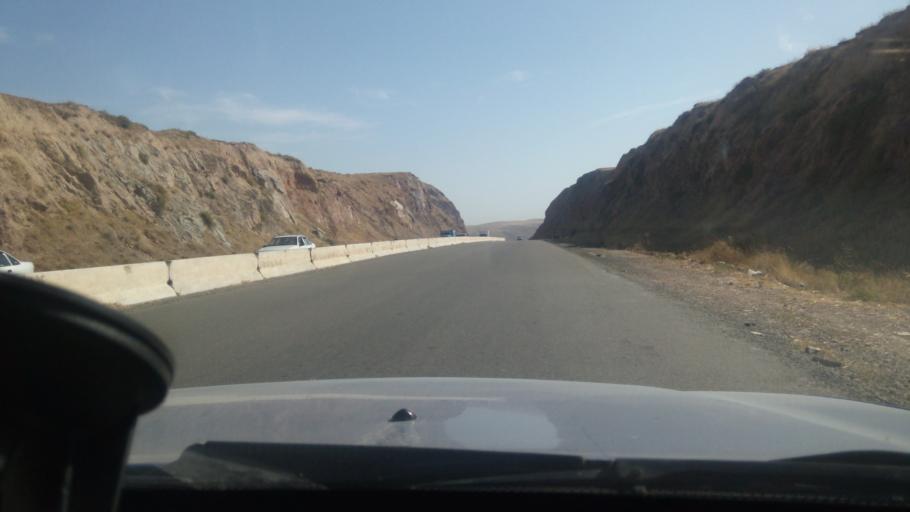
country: UZ
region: Jizzax
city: Jizzax
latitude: 40.0479
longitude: 67.6768
